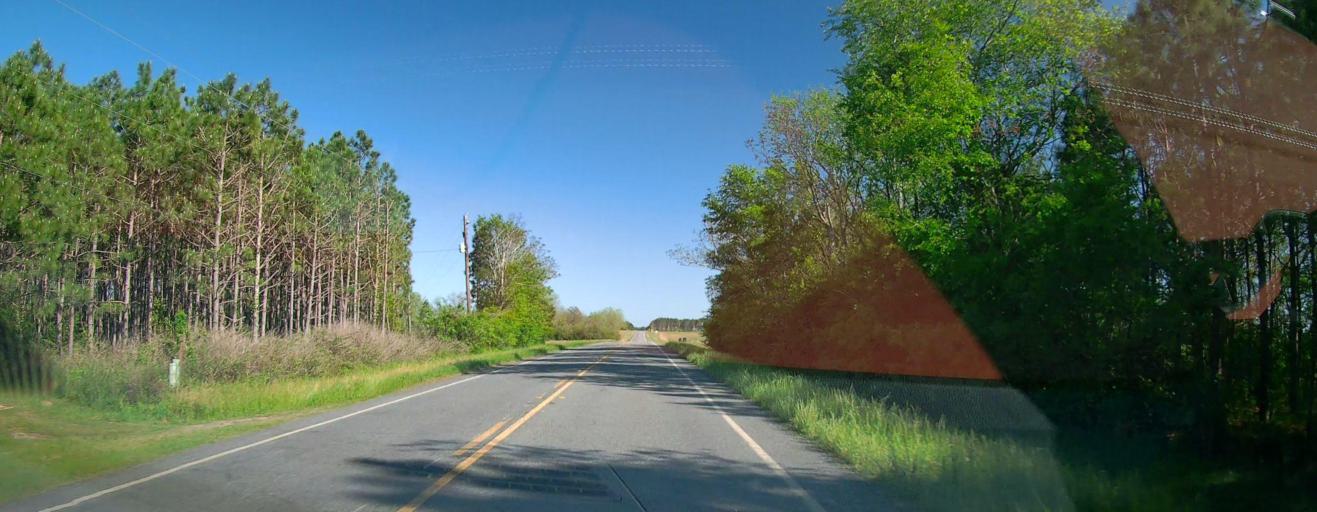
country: US
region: Georgia
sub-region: Wilcox County
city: Rochelle
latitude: 31.9943
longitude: -83.4720
